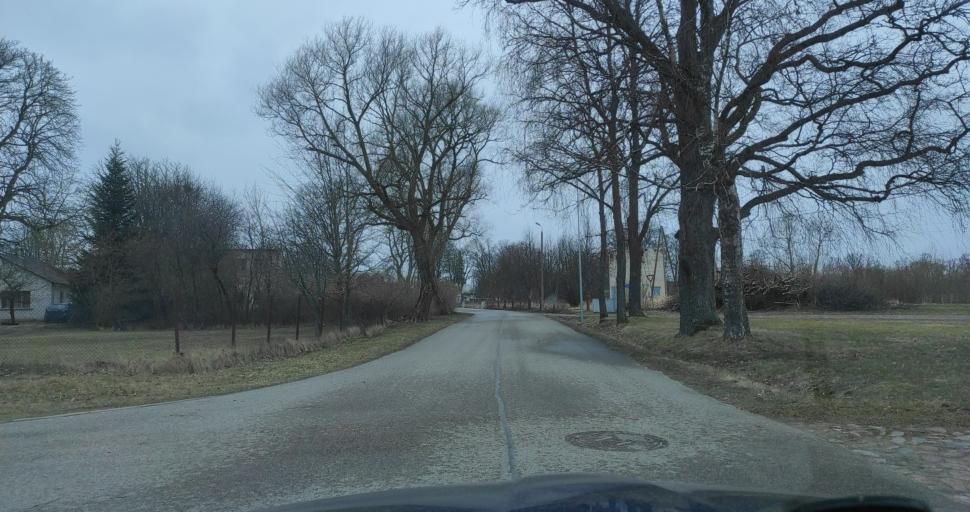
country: LV
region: Ventspils Rajons
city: Piltene
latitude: 57.2252
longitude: 21.6801
